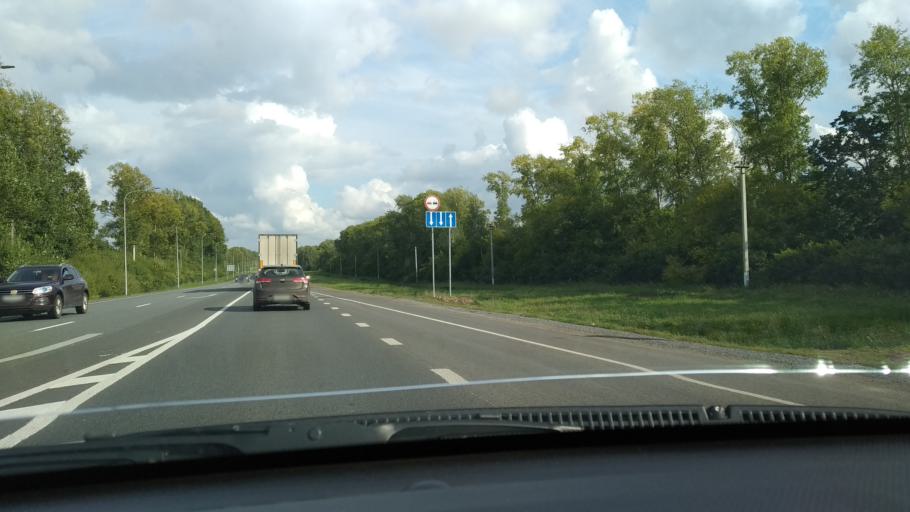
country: RU
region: Tatarstan
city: Stolbishchi
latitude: 55.6550
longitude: 49.3139
